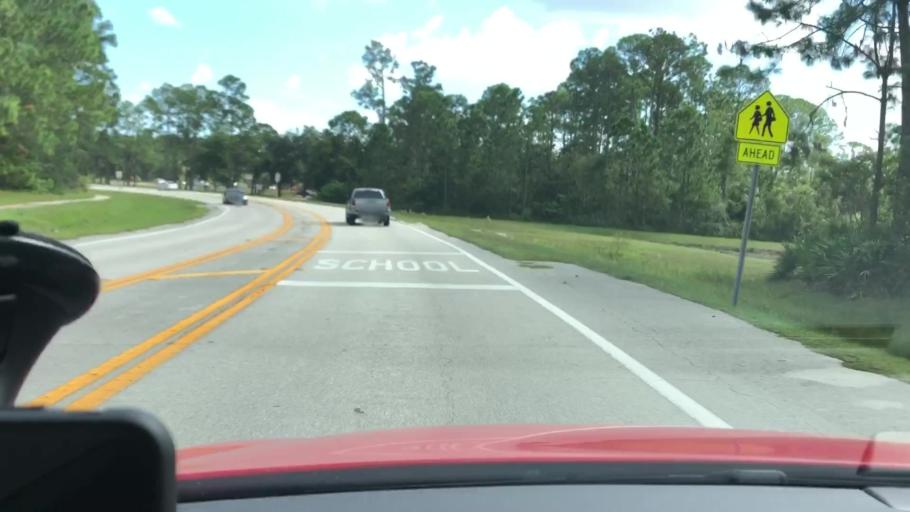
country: US
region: Florida
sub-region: Volusia County
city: Daytona Beach
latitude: 29.1996
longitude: -81.0768
